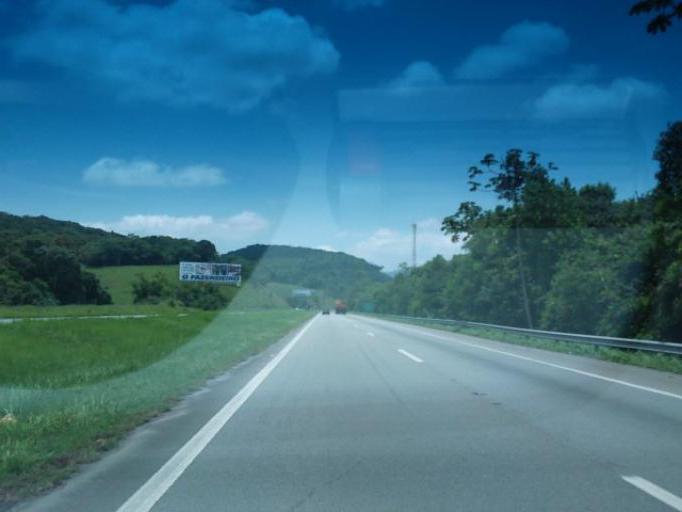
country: BR
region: Sao Paulo
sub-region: Miracatu
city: Miracatu
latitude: -24.2151
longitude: -47.3682
